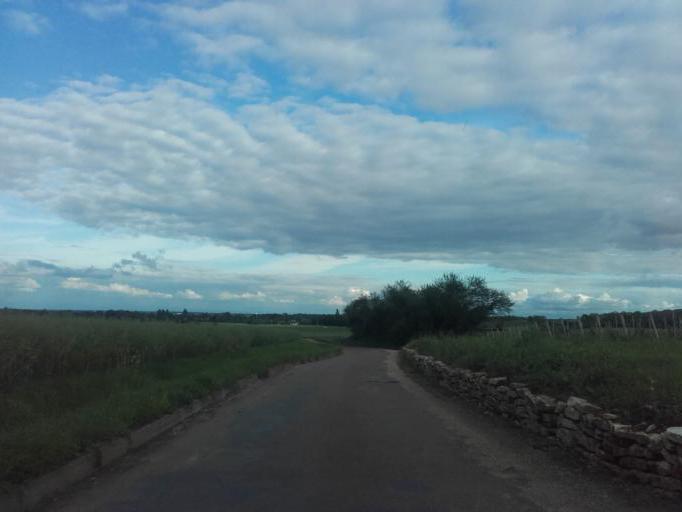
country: FR
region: Bourgogne
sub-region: Departement de Saone-et-Loire
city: Rully
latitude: 46.8671
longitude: 4.7465
